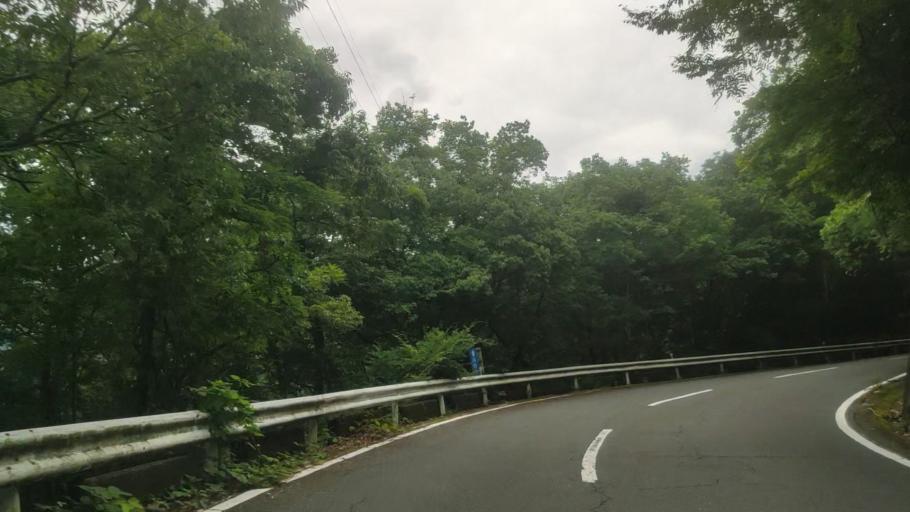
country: JP
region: Wakayama
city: Koya
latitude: 34.2363
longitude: 135.5478
